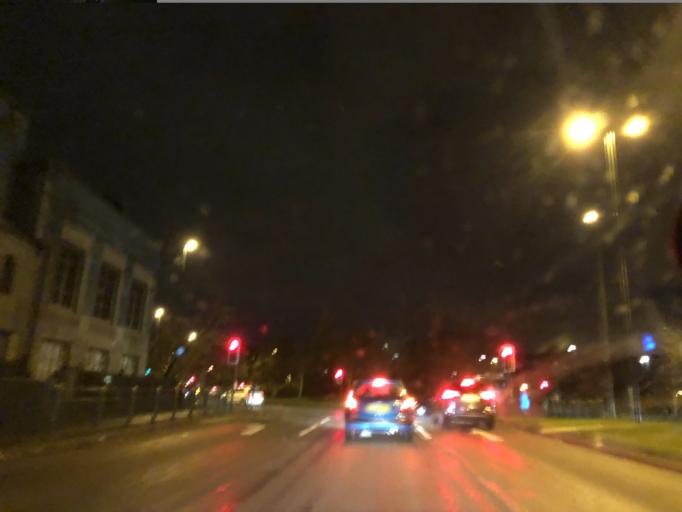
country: GB
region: England
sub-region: Borough of Oldham
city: Oldham
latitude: 53.5369
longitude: -2.1158
